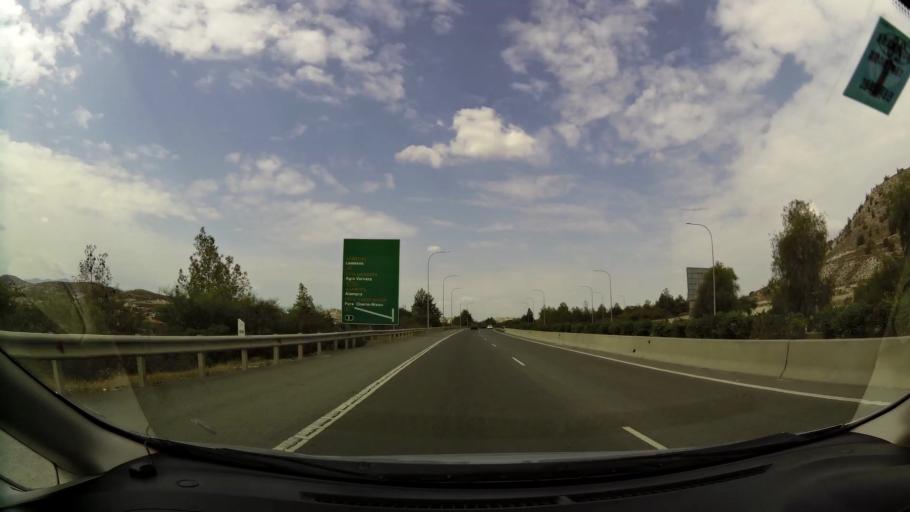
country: CY
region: Lefkosia
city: Alampra
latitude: 35.0010
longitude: 33.3998
